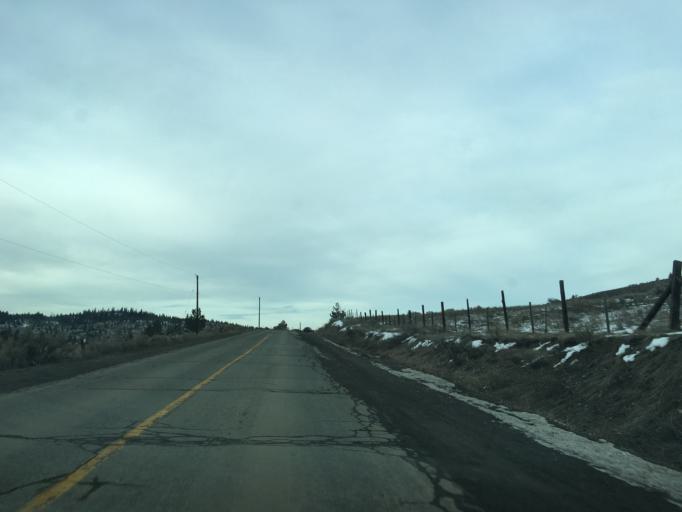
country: CA
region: British Columbia
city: Kamloops
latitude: 50.6218
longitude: -120.4431
